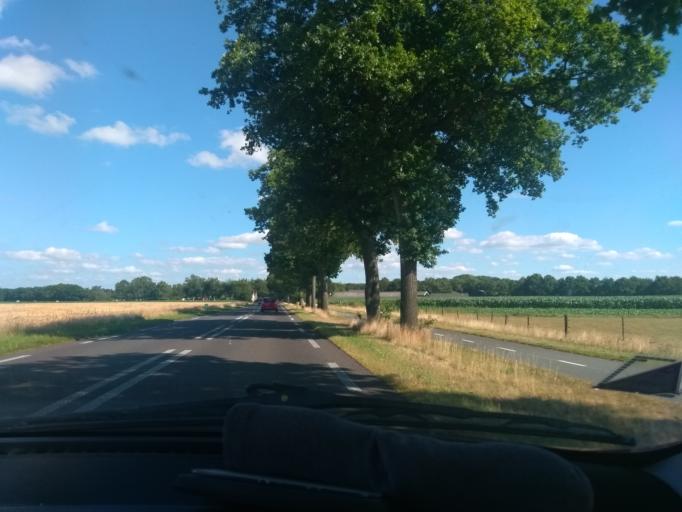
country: NL
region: Drenthe
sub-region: Gemeente Tynaarlo
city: Vries
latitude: 53.0858
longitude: 6.5642
